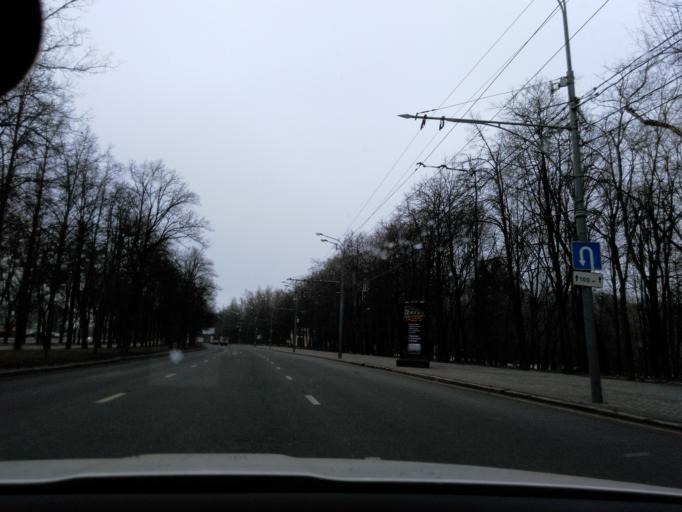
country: RU
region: Moscow
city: Vorob'yovo
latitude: 55.7122
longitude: 37.5375
